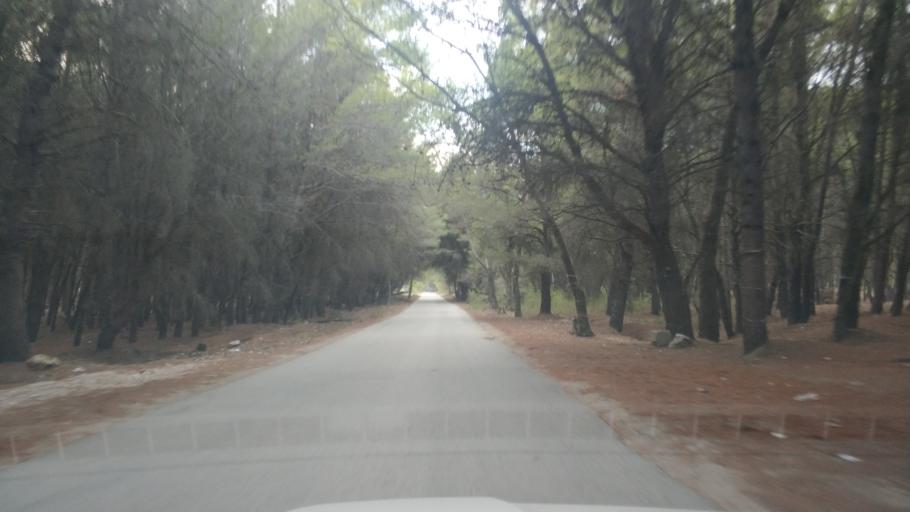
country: AL
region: Vlore
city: Vlore
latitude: 40.4894
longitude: 19.4406
